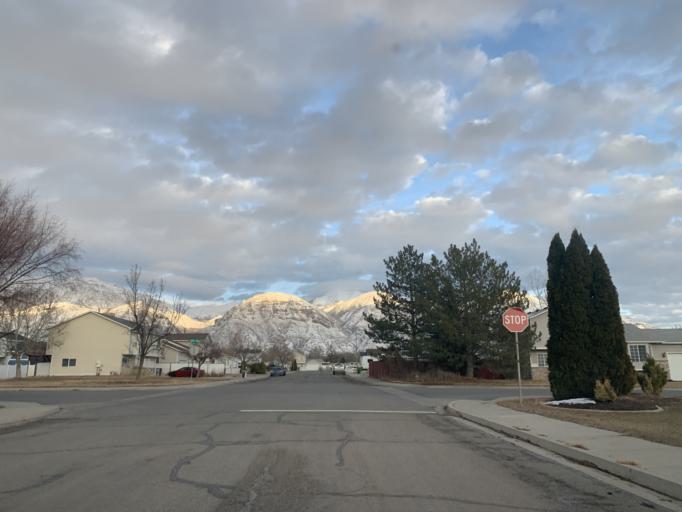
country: US
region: Utah
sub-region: Utah County
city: Provo
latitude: 40.2463
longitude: -111.7082
